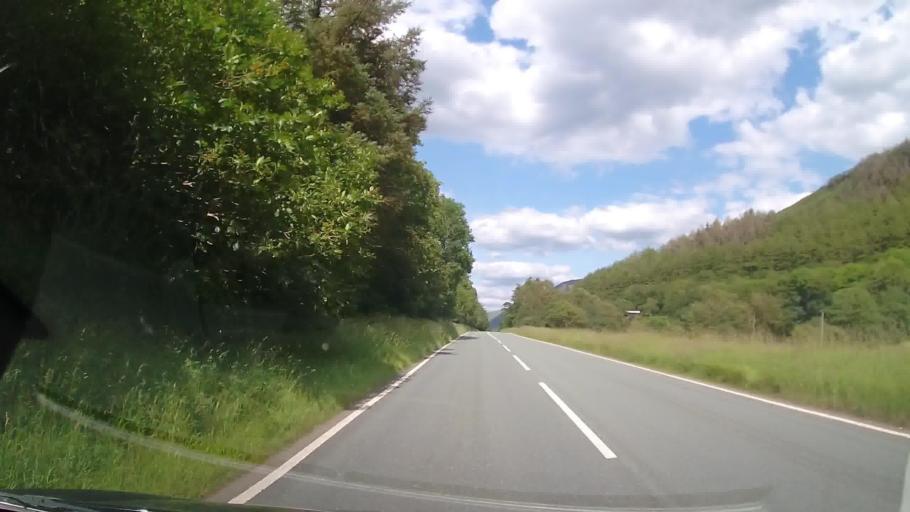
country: GB
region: Wales
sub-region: Gwynedd
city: Barmouth
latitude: 52.6377
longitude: -3.9700
